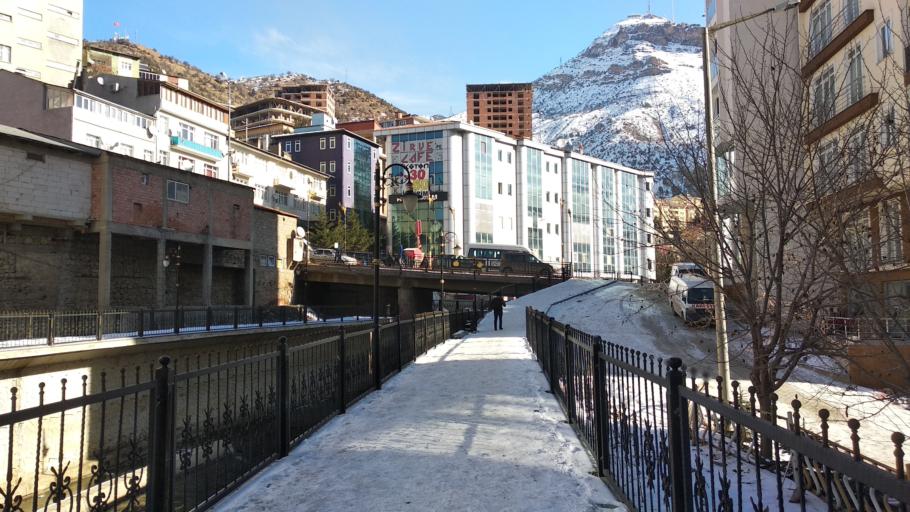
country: TR
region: Gumushane
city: Gumushkhane
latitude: 40.4585
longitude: 39.4821
